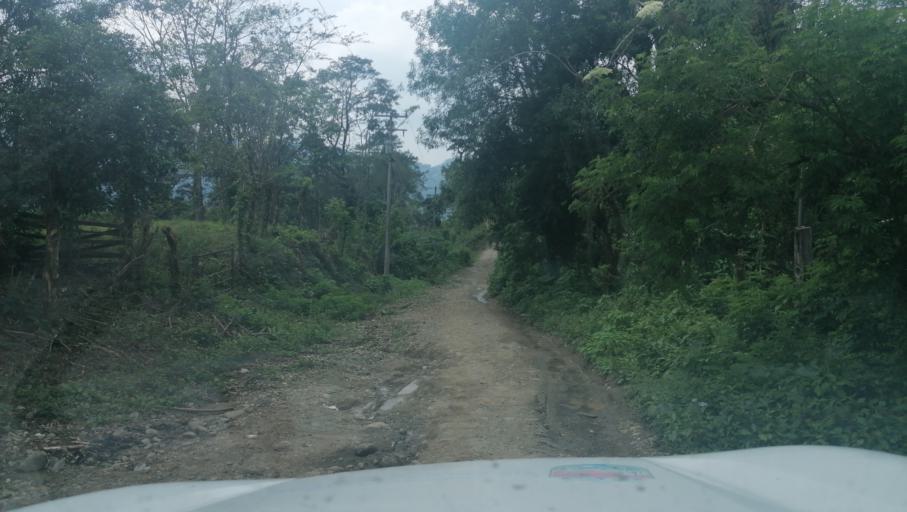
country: MX
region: Chiapas
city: Ostuacan
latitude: 17.3616
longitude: -93.3253
